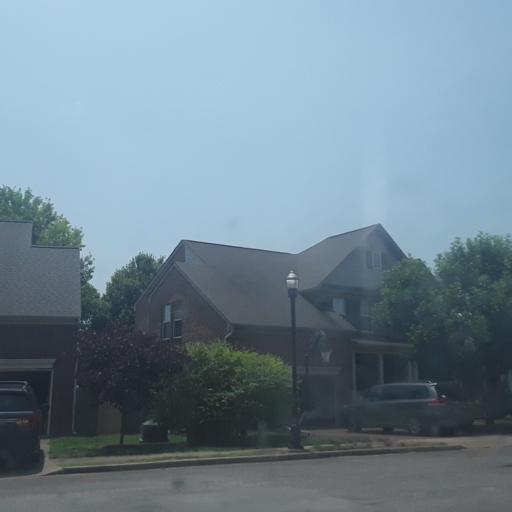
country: US
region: Tennessee
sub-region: Williamson County
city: Brentwood
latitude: 36.0555
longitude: -86.7505
